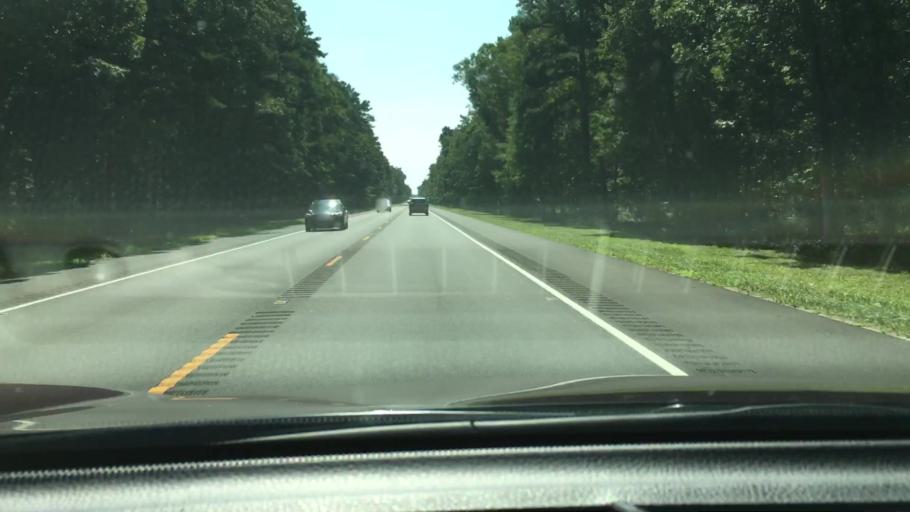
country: US
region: New Jersey
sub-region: Cape May County
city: Woodbine
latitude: 39.3416
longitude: -74.8943
